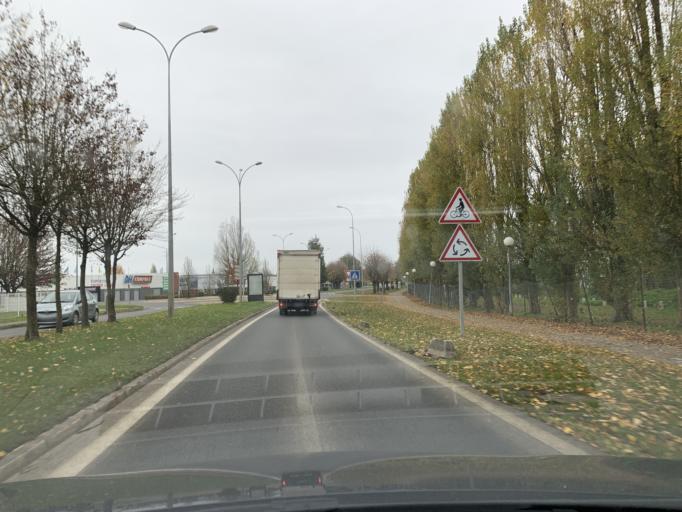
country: FR
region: Nord-Pas-de-Calais
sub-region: Departement du Nord
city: Neuville-Saint-Remy
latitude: 50.1926
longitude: 3.2127
